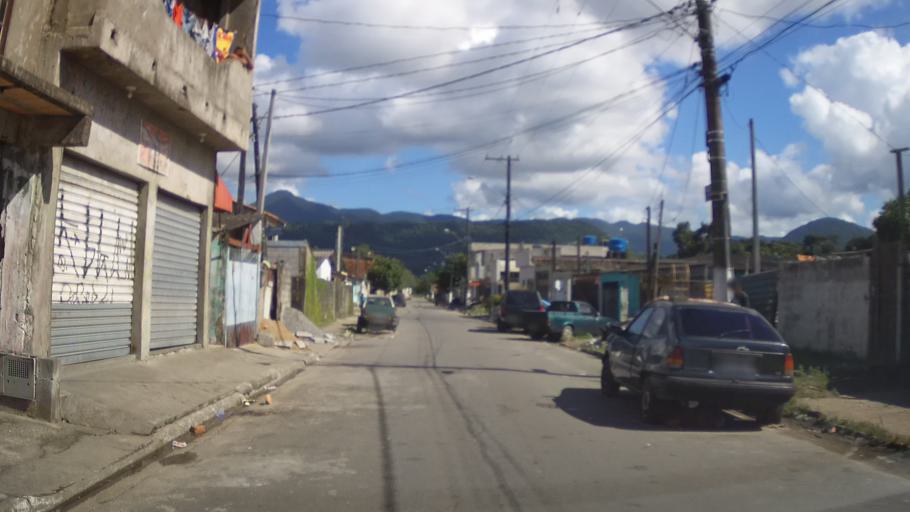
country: BR
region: Sao Paulo
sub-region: Praia Grande
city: Praia Grande
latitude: -24.0183
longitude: -46.5118
